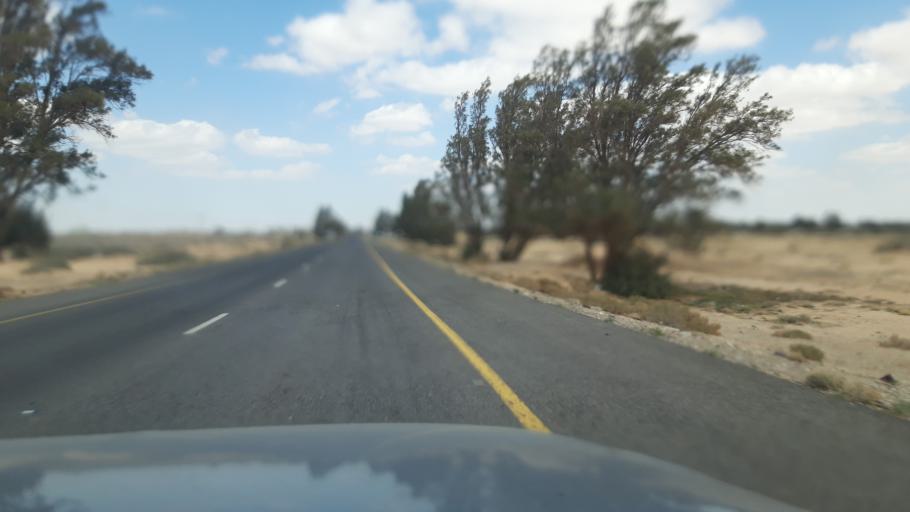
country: JO
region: Amman
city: Al Azraq ash Shamali
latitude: 31.8206
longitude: 36.8085
